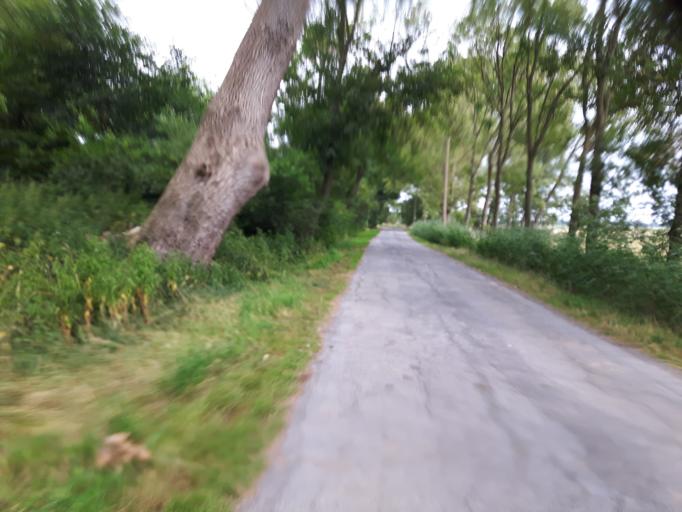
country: DE
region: Lower Saxony
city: Varel
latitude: 53.3666
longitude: 8.2074
